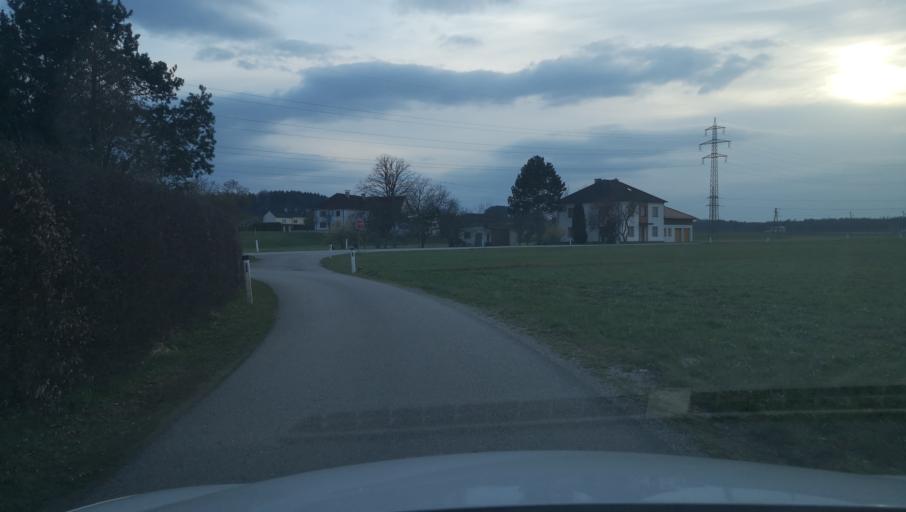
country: AT
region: Lower Austria
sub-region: Politischer Bezirk Amstetten
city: Amstetten
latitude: 48.1063
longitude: 14.8909
